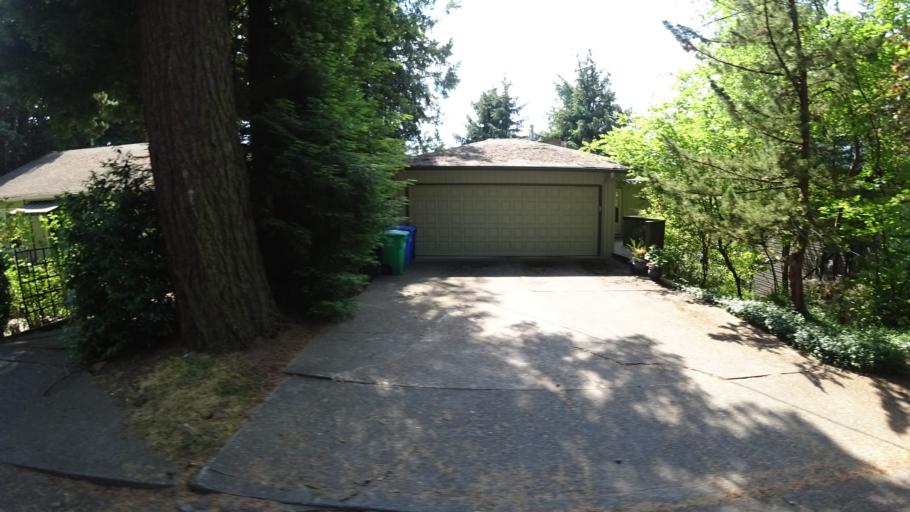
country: US
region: Oregon
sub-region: Multnomah County
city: Portland
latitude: 45.4927
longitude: -122.7046
